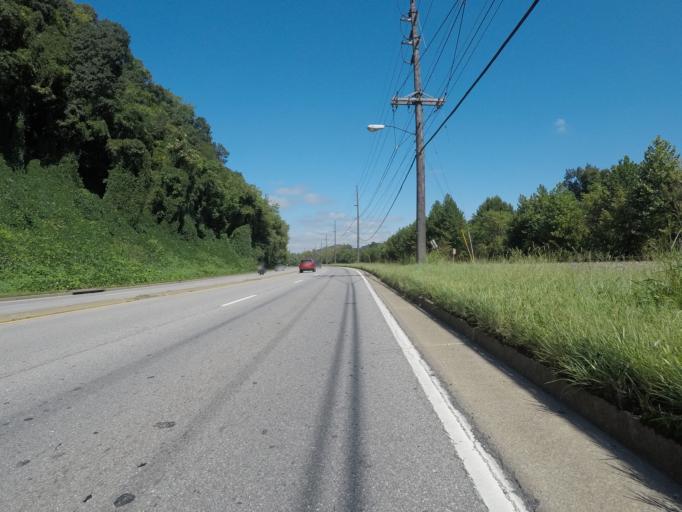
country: US
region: Kentucky
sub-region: Boyd County
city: Ashland
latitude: 38.4579
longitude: -82.6128
